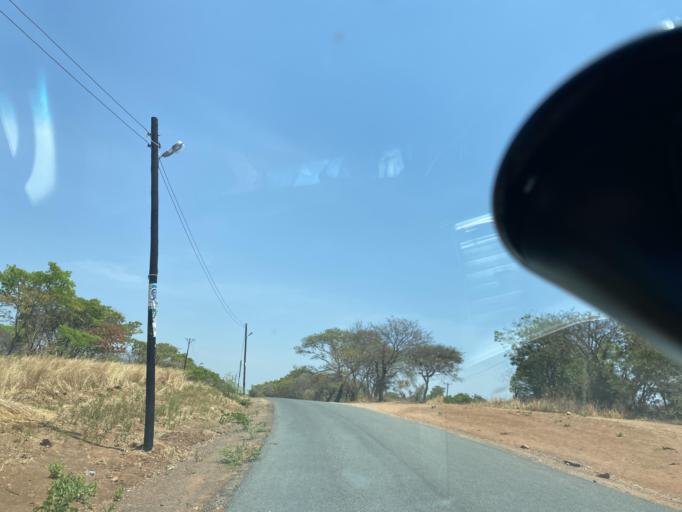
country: ZM
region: Lusaka
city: Kafue
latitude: -15.8656
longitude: 28.4417
